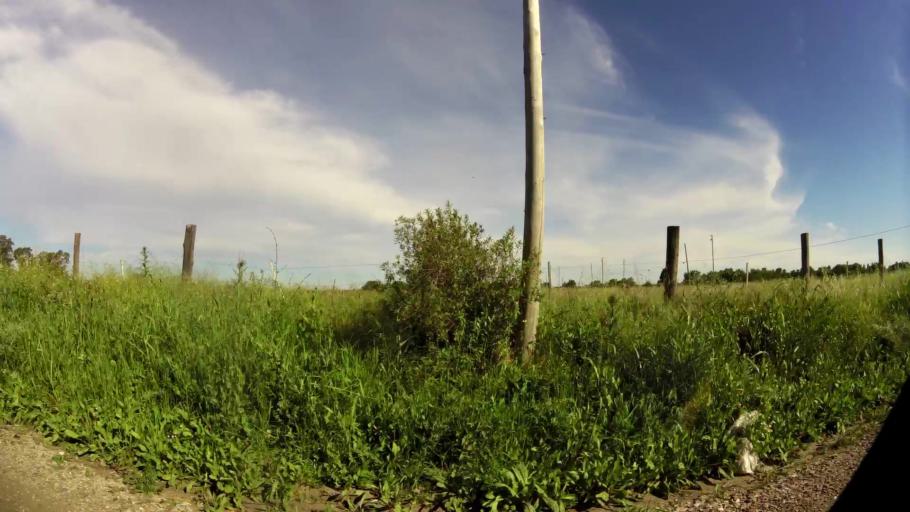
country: AR
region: Buenos Aires
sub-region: Partido de Almirante Brown
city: Adrogue
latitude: -34.8259
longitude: -58.3378
